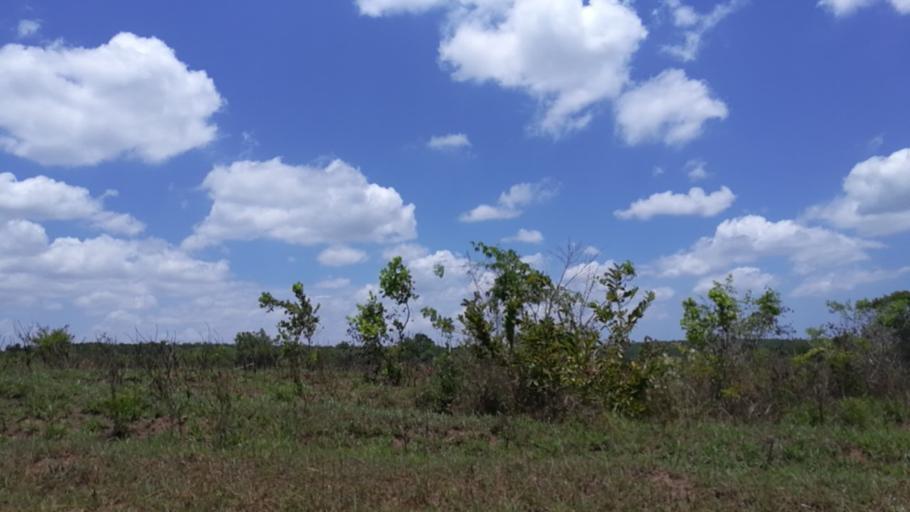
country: KE
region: Kwale
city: Kwale
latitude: -4.2335
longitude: 39.4273
